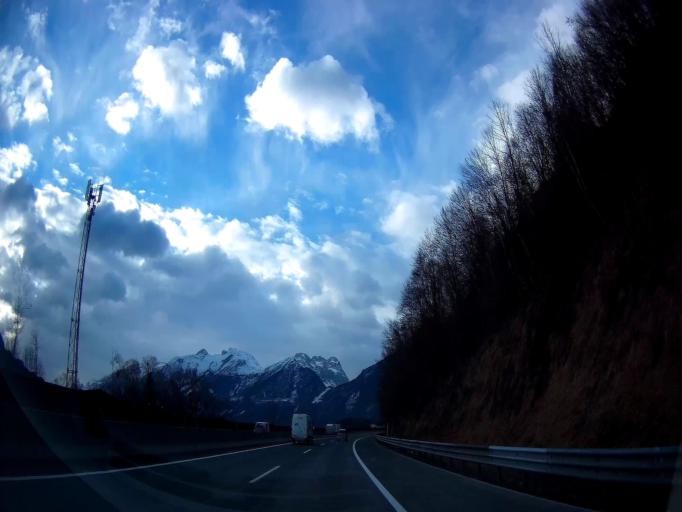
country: AT
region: Salzburg
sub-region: Politischer Bezirk Hallein
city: Kuchl
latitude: 47.6217
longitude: 13.1380
